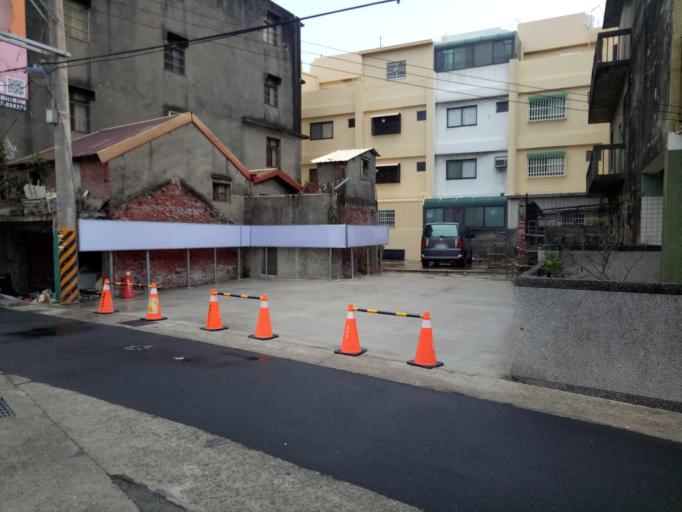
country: TW
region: Taiwan
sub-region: Changhua
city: Chang-hua
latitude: 24.2463
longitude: 120.5397
